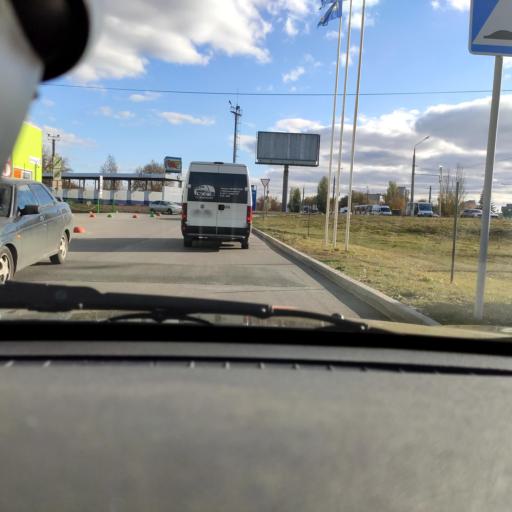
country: RU
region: Samara
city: Tol'yatti
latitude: 53.5392
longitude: 49.3900
